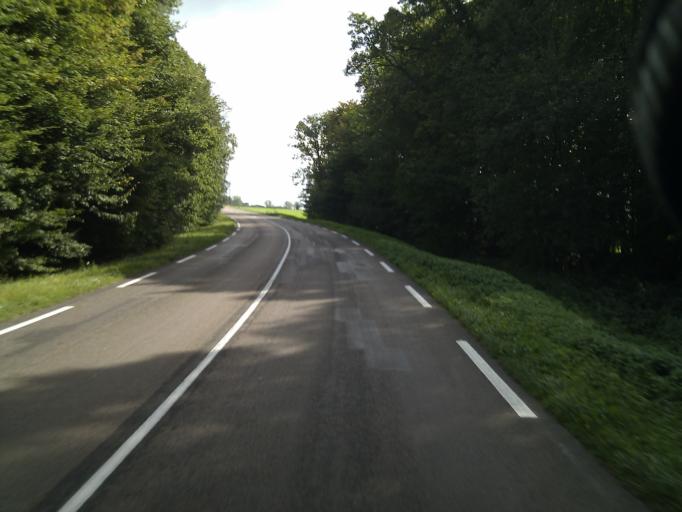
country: FR
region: Bourgogne
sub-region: Departement de la Cote-d'Or
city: Semur-en-Auxois
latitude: 47.4466
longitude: 4.3016
